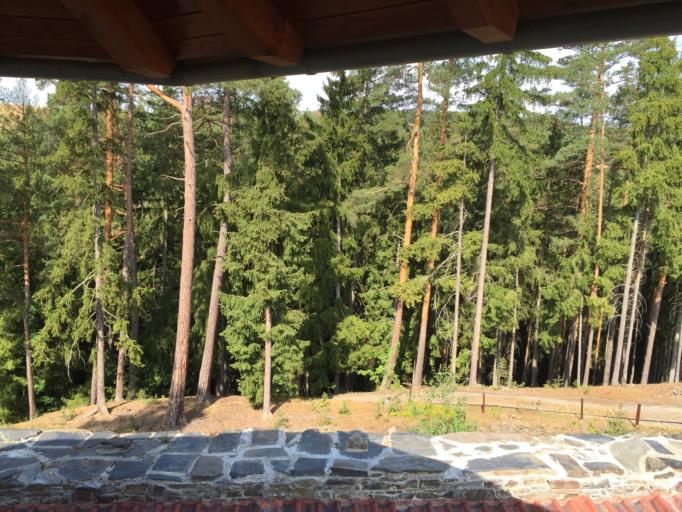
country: DE
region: Thuringia
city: Altenbeuthen
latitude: 50.5747
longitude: 11.6081
